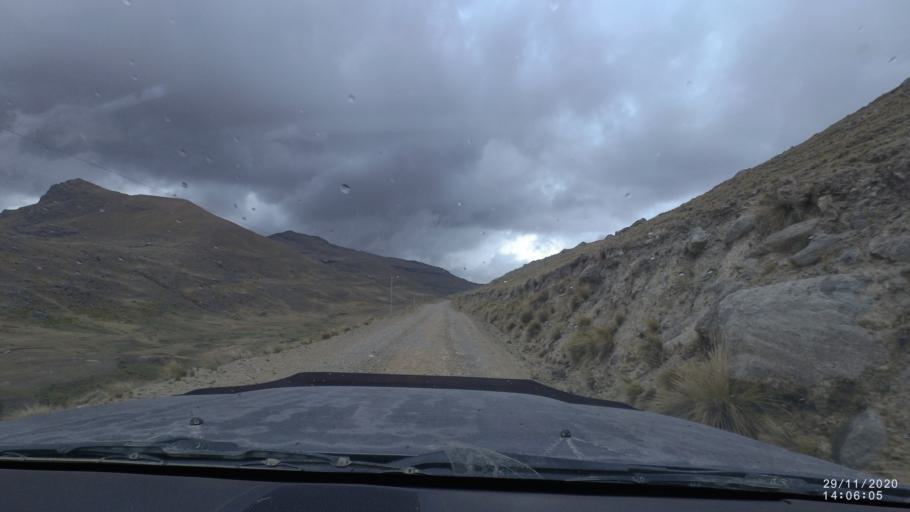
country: BO
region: Cochabamba
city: Sipe Sipe
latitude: -17.2111
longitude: -66.3773
